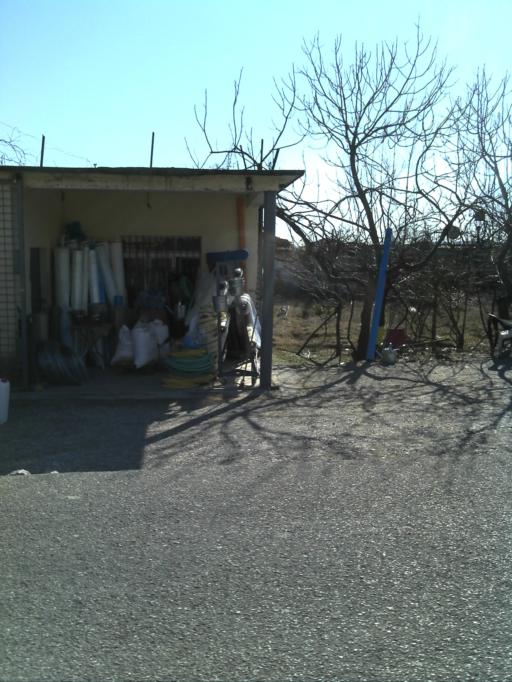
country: AL
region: Shkoder
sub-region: Rrethi i Shkodres
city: Dajc
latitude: 42.0154
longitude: 19.4378
